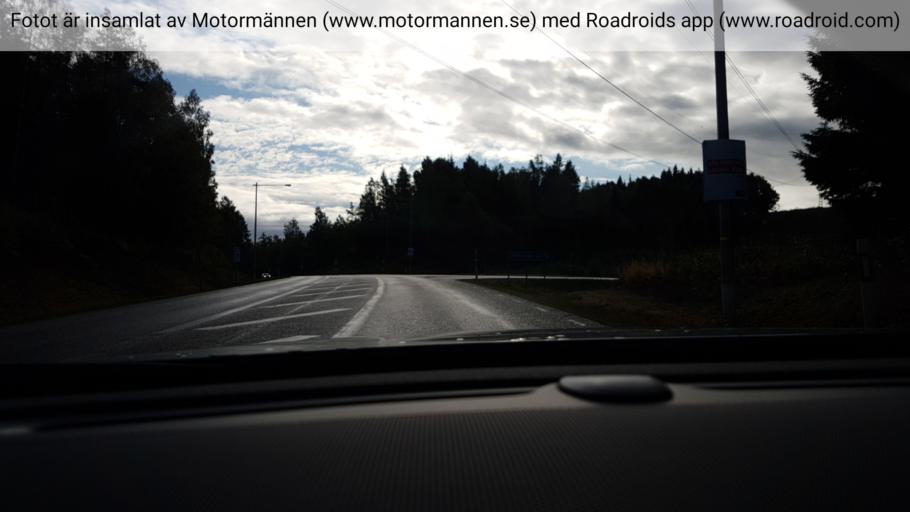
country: SE
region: Vaestra Goetaland
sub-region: Harryda Kommun
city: Hindas
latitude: 57.6220
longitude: 12.4207
